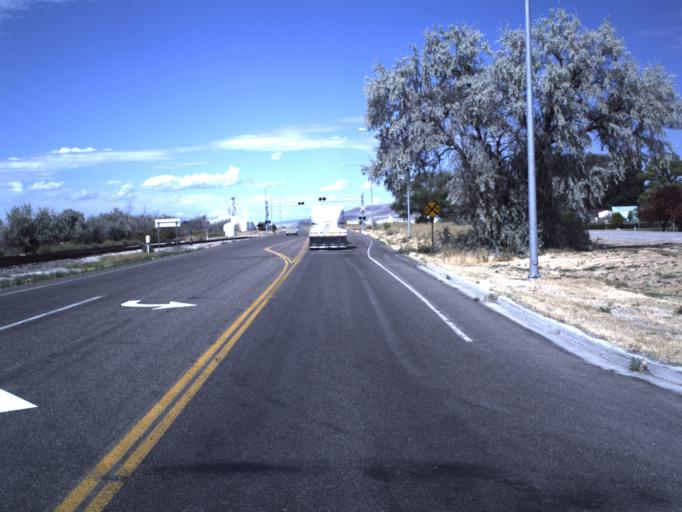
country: US
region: Utah
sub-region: Box Elder County
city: Honeyville
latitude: 41.5517
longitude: -112.1129
